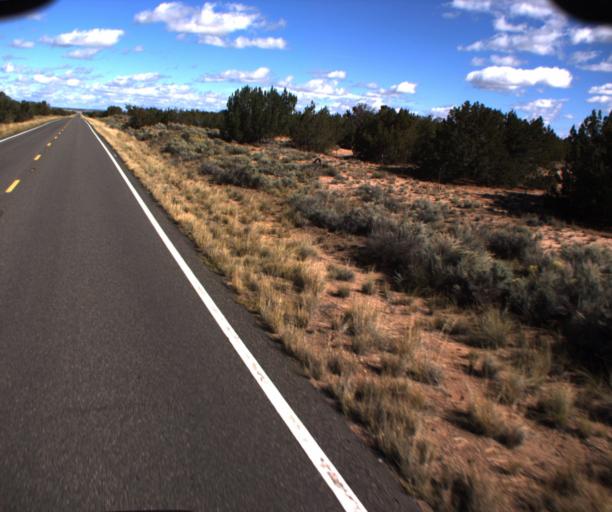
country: US
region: Arizona
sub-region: Apache County
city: Saint Johns
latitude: 34.8686
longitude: -109.2378
